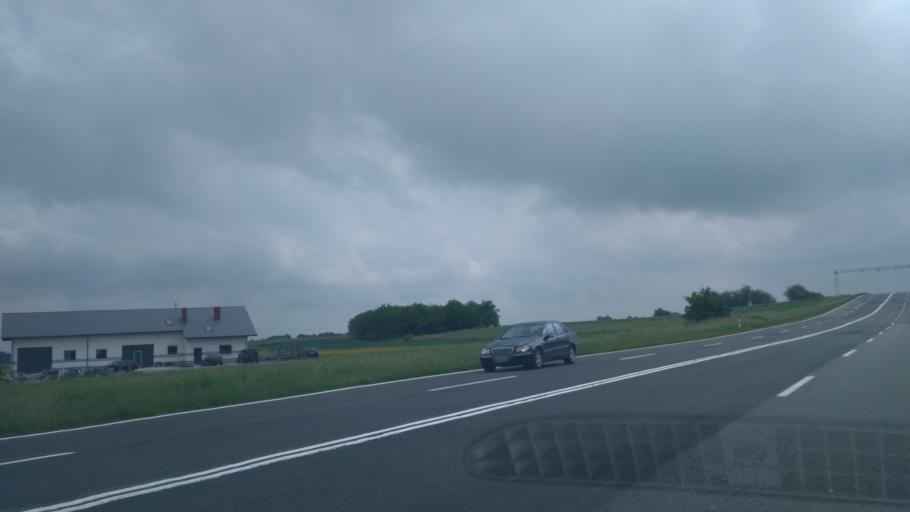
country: PL
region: Subcarpathian Voivodeship
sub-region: Powiat przeworski
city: Rozborz
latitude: 50.0495
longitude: 22.5300
